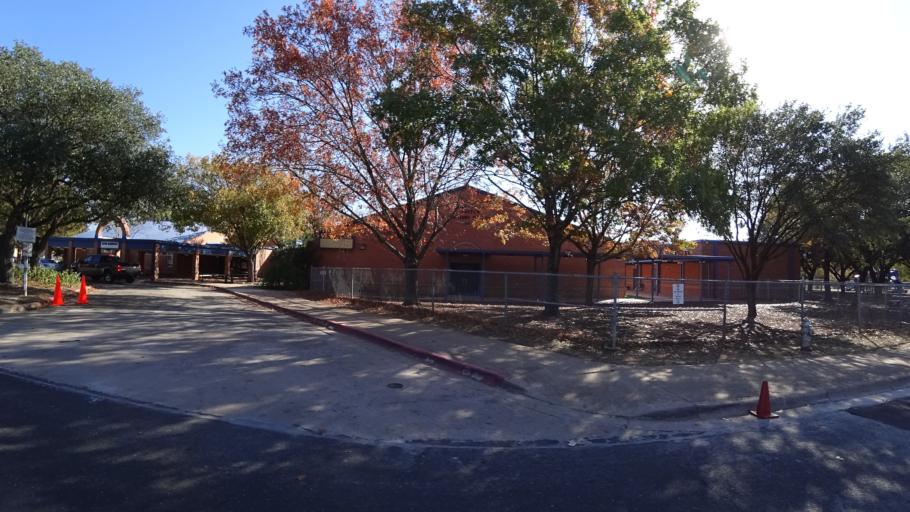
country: US
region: Texas
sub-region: Travis County
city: Barton Creek
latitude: 30.2320
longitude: -97.8462
